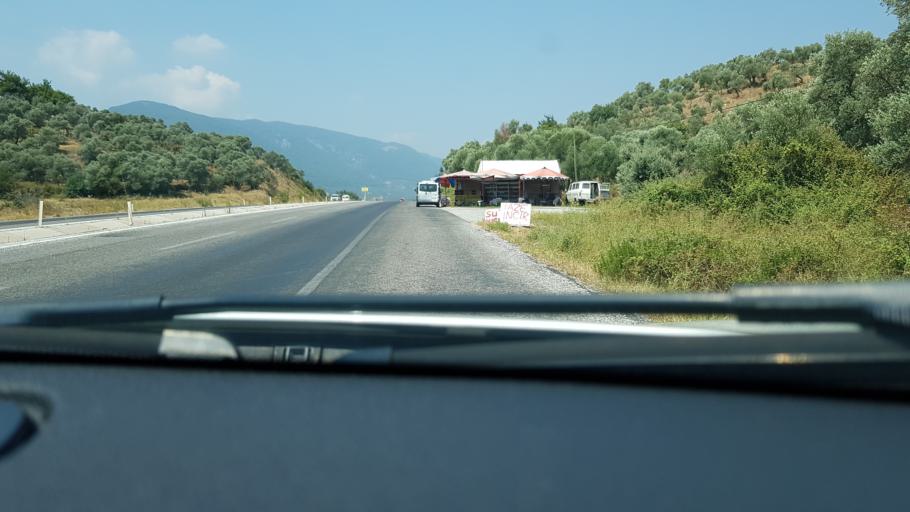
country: TR
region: Mugla
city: Selimiye
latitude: 37.4114
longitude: 27.6322
